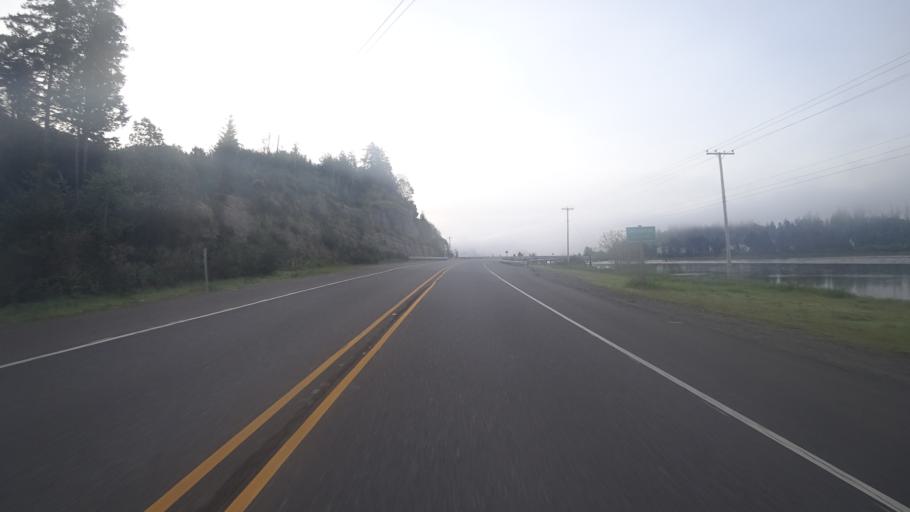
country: US
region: Oregon
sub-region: Douglas County
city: Reedsport
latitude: 43.7203
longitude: -124.1045
